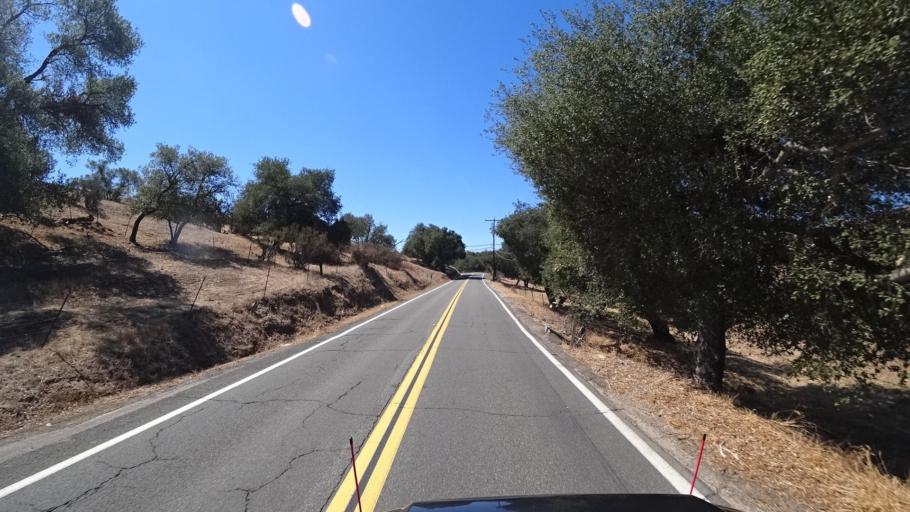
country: US
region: California
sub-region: San Diego County
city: Ramona
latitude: 33.0470
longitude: -116.8191
